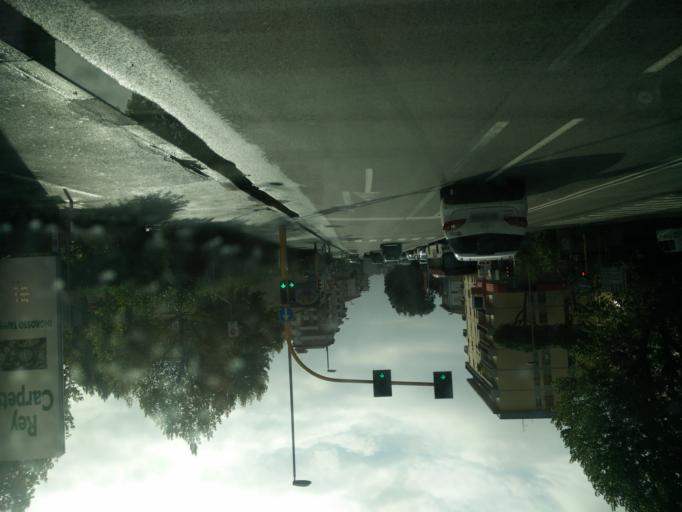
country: IT
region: Tuscany
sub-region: Province of Florence
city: Florence
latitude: 43.7940
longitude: 11.2106
